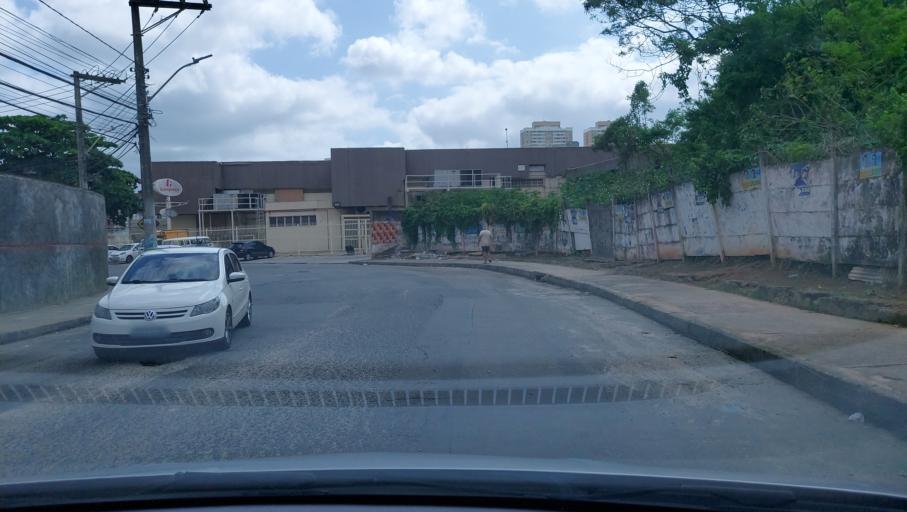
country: BR
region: Bahia
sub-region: Salvador
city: Salvador
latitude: -12.9731
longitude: -38.4354
